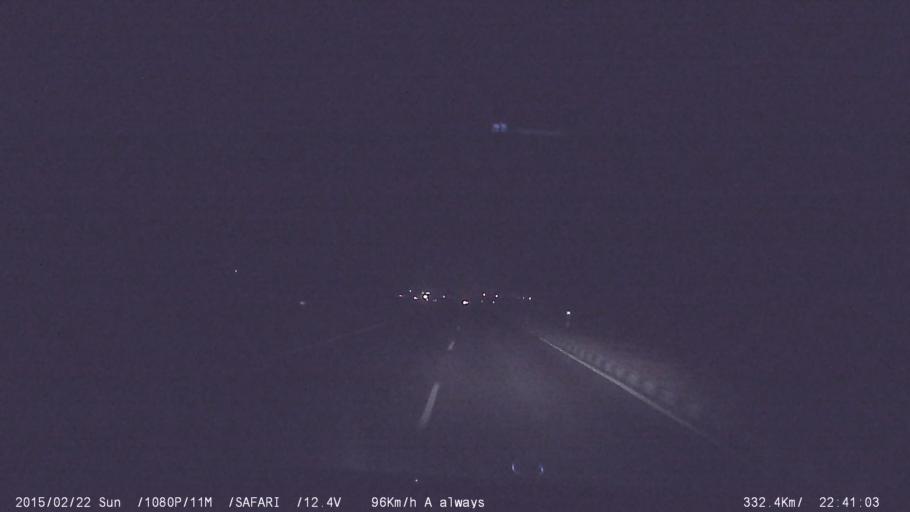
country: IN
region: Tamil Nadu
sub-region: Namakkal
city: Velur
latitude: 11.1809
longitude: 78.0663
